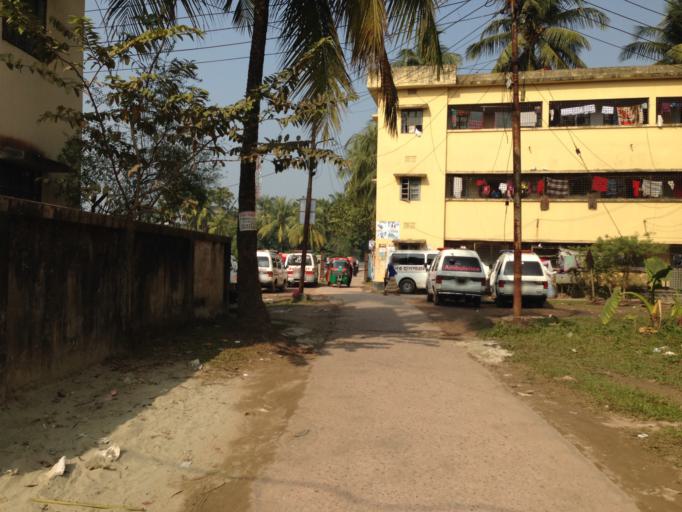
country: BD
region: Chittagong
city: Lakshmipur
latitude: 22.9350
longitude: 90.8331
